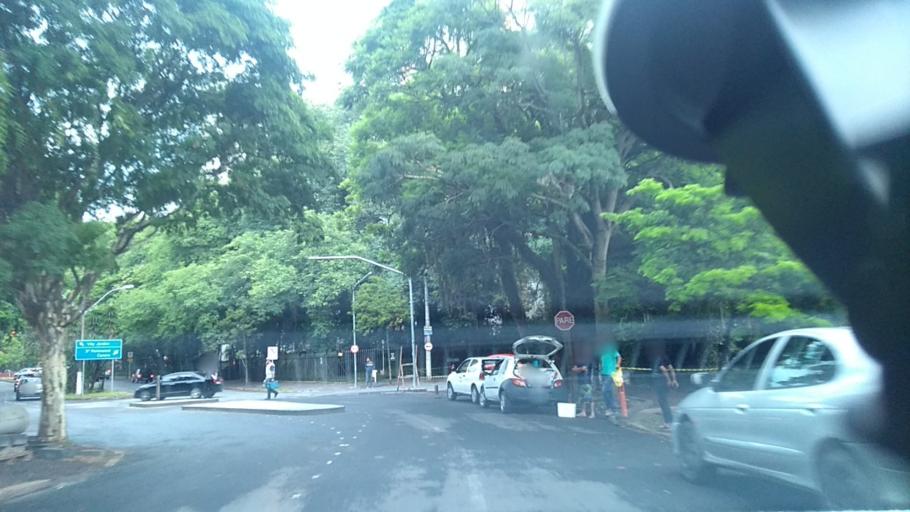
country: BR
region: Rio Grande do Sul
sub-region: Porto Alegre
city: Porto Alegre
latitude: -30.0274
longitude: -51.1764
